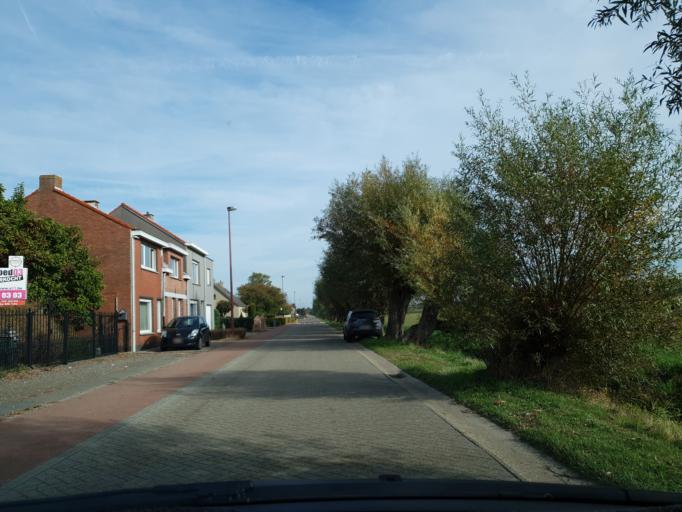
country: BE
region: Flanders
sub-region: Provincie Antwerpen
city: Stabroek
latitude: 51.3315
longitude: 4.3933
